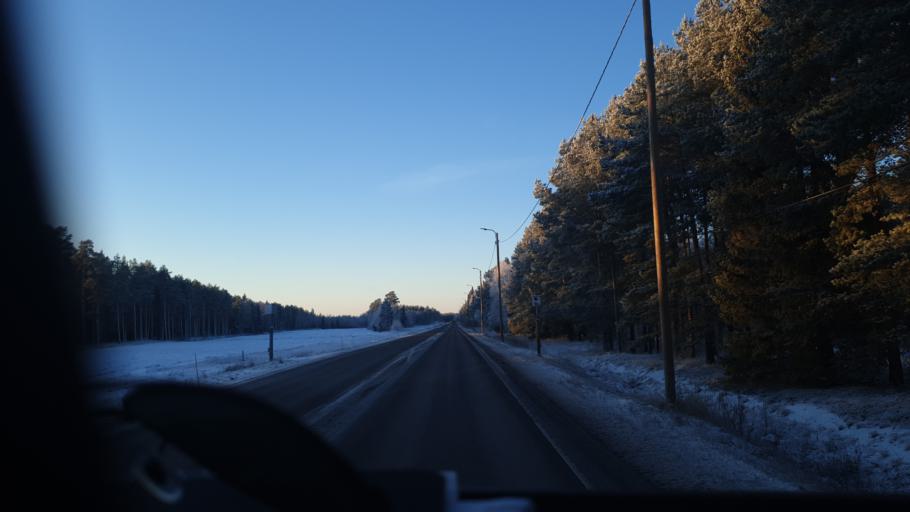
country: FI
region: Northern Ostrobothnia
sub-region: Ylivieska
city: Kalajoki
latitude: 64.2463
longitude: 23.8768
